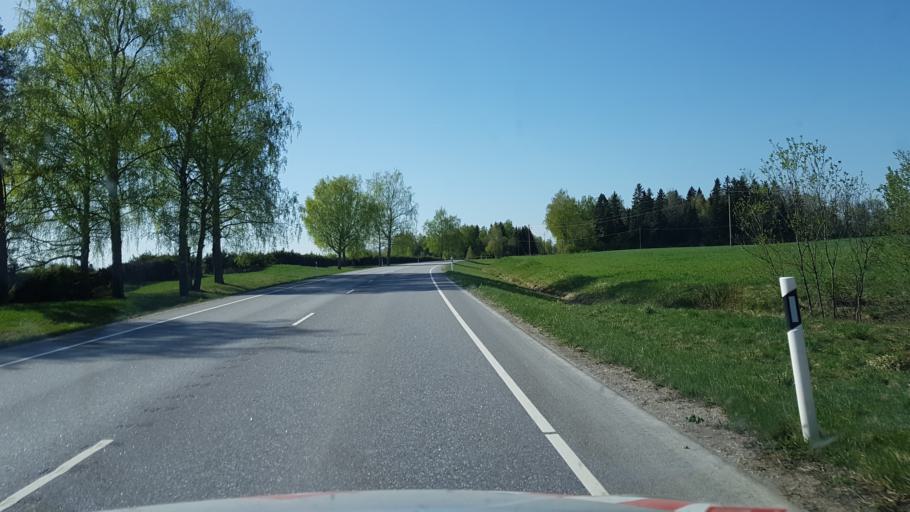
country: EE
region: Viljandimaa
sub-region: Karksi vald
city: Karksi-Nuia
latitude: 58.1049
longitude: 25.5262
